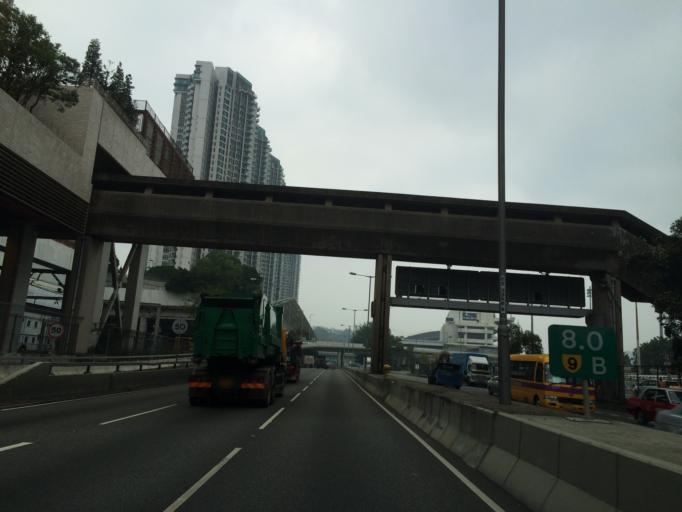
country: HK
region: Sha Tin
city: Sha Tin
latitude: 22.3971
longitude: 114.2010
